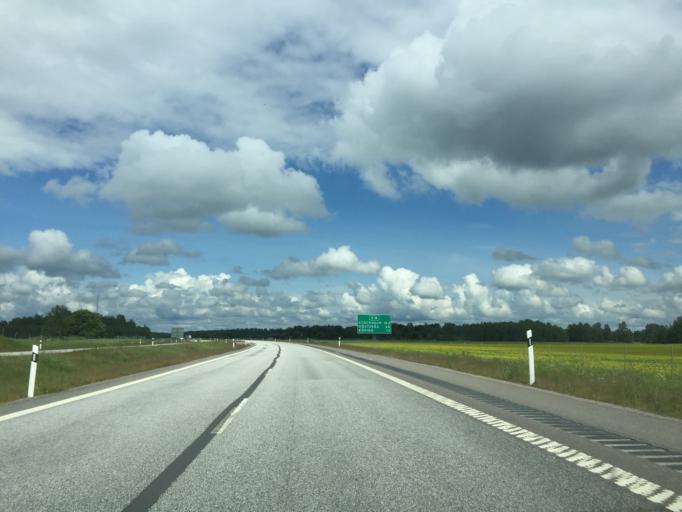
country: SE
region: Vaestmanland
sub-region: Arboga Kommun
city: Arboga
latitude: 59.4394
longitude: 15.9001
